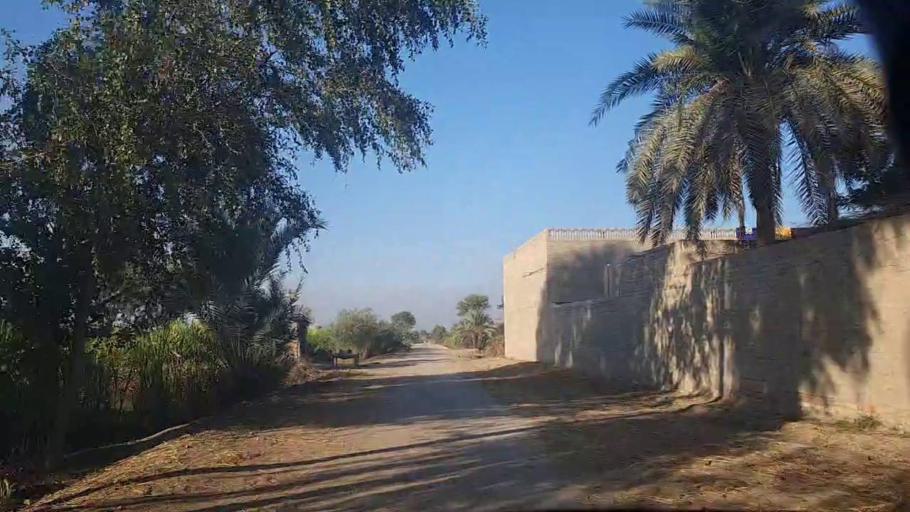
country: PK
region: Sindh
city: Sobhadero
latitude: 27.4185
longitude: 68.4232
